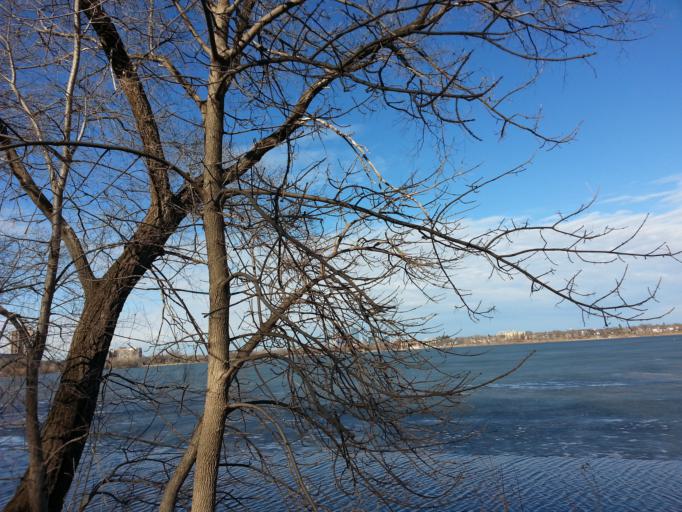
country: US
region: Minnesota
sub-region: Hennepin County
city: Saint Louis Park
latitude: 44.9398
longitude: -93.3199
